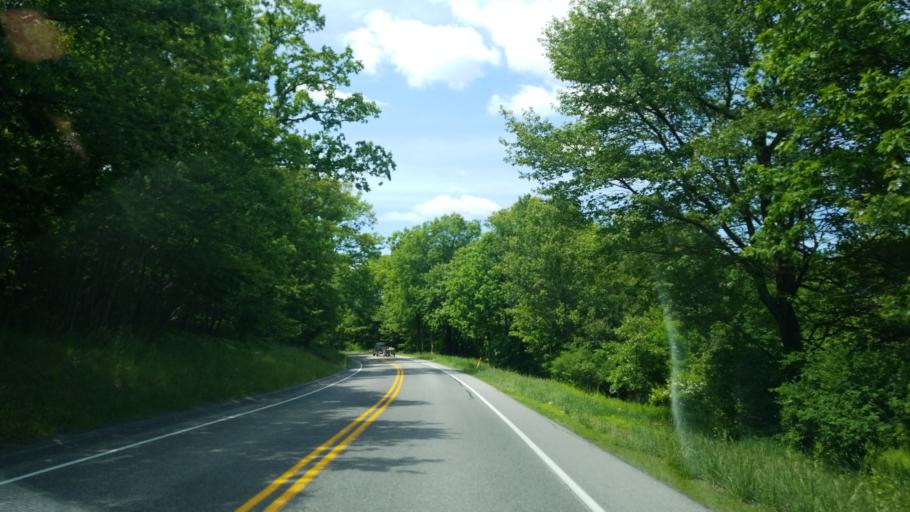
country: US
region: Pennsylvania
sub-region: Blair County
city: Tipton
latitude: 40.7110
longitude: -78.3160
